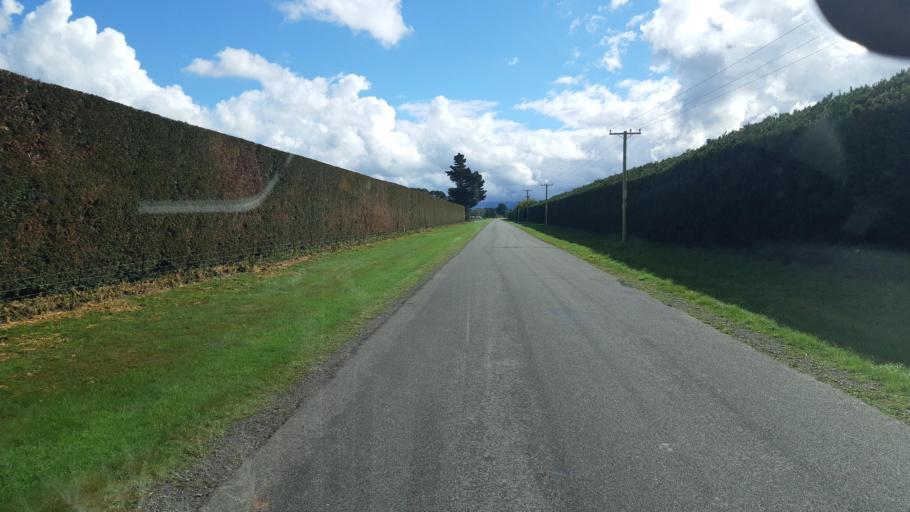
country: NZ
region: Canterbury
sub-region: Waimakariri District
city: Oxford
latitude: -43.3185
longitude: 172.1803
